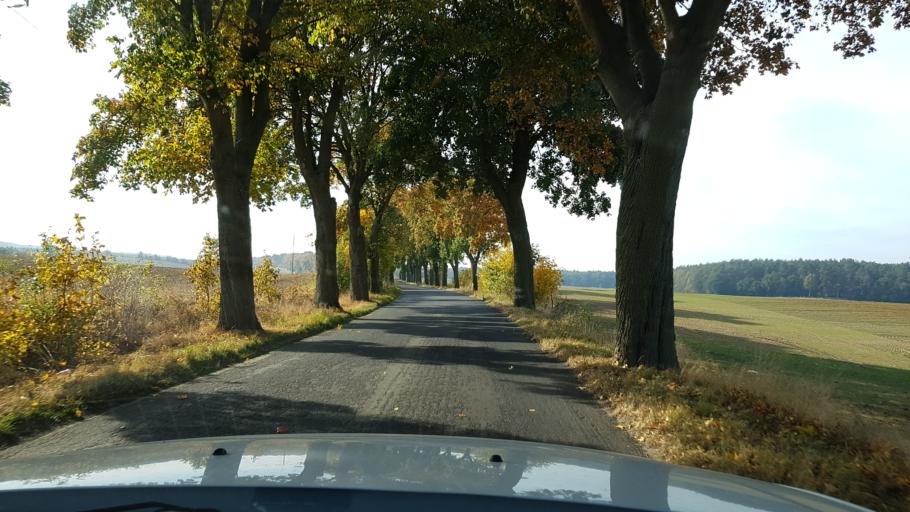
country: PL
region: West Pomeranian Voivodeship
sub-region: Powiat mysliborski
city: Nowogrodek Pomorski
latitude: 52.9539
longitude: 15.1035
